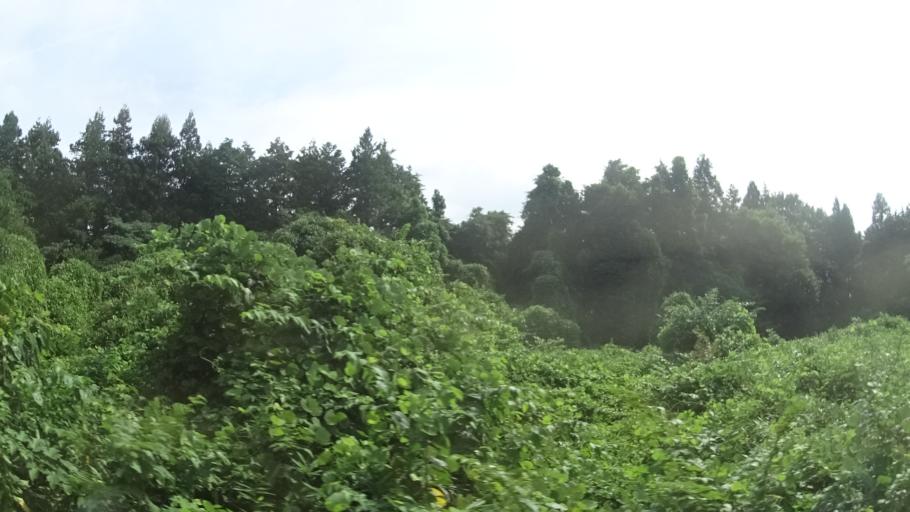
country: JP
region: Tochigi
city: Kanuma
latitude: 36.6213
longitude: 139.7344
